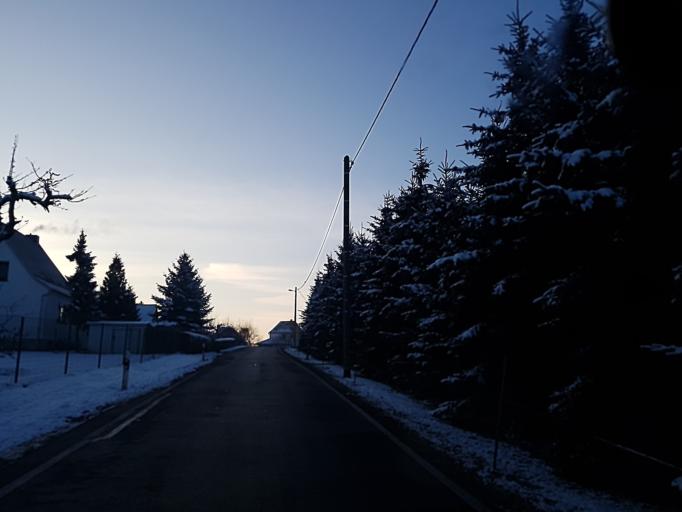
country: DE
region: Saxony
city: Grossweitzschen
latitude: 51.1774
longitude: 13.0413
